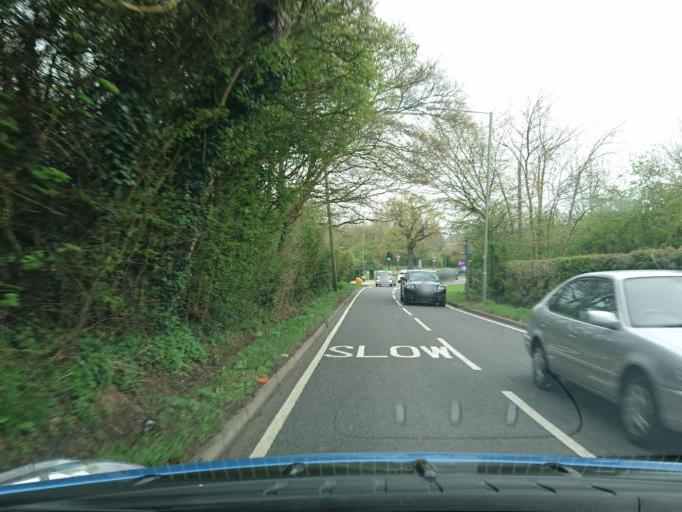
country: GB
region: England
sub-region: Greater London
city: Barnet
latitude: 51.6385
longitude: -0.1983
